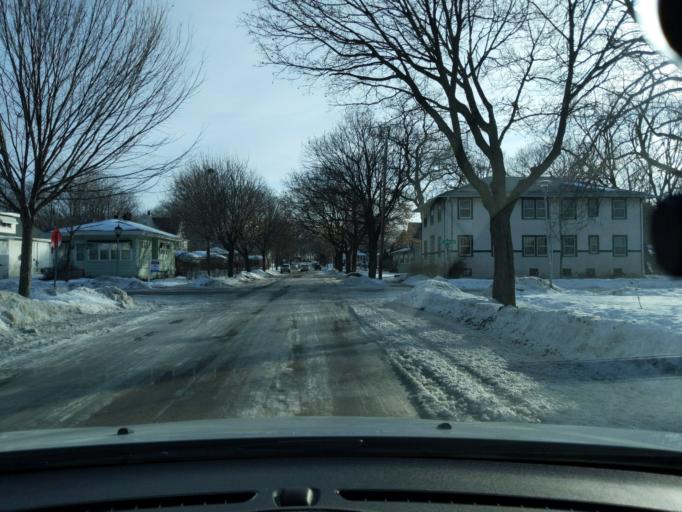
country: US
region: Minnesota
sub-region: Ramsey County
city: Lauderdale
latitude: 44.9861
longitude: -93.2233
